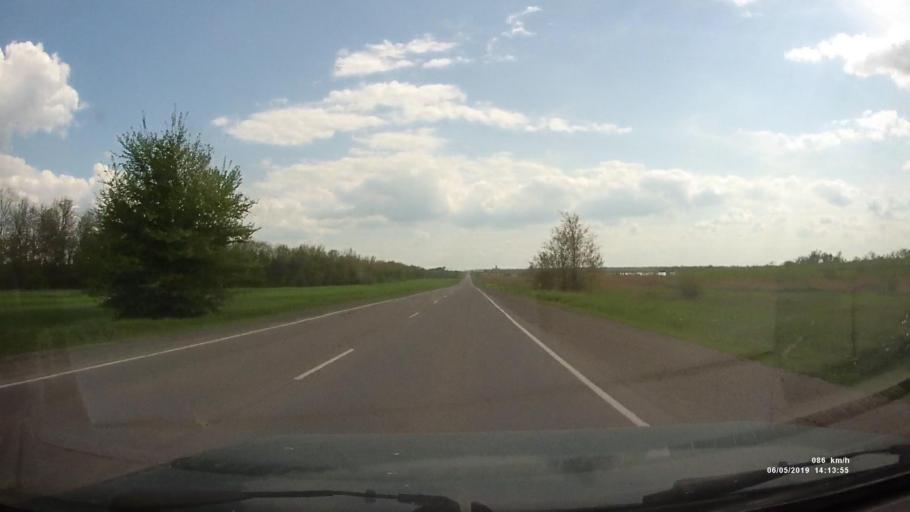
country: RU
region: Rostov
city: Kamenolomni
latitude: 47.6548
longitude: 40.2945
